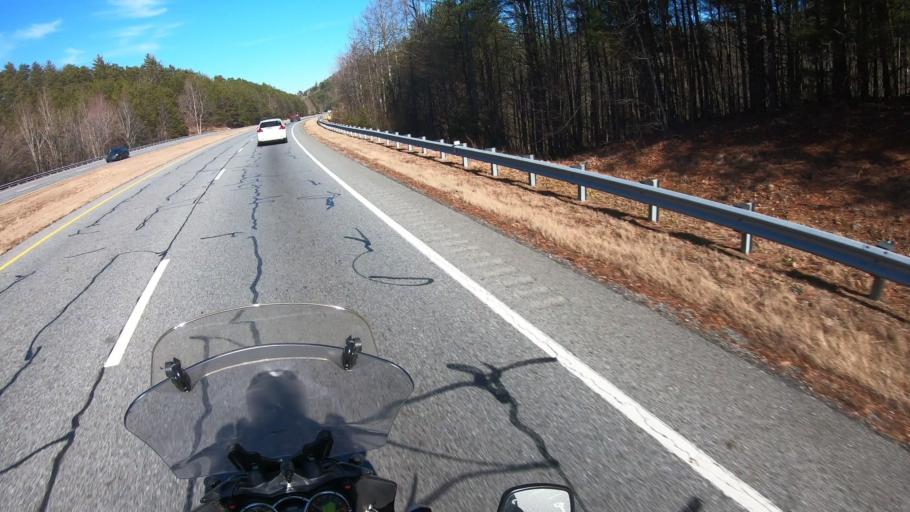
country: US
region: Georgia
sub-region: Gilmer County
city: Ellijay
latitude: 34.7560
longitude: -84.4059
